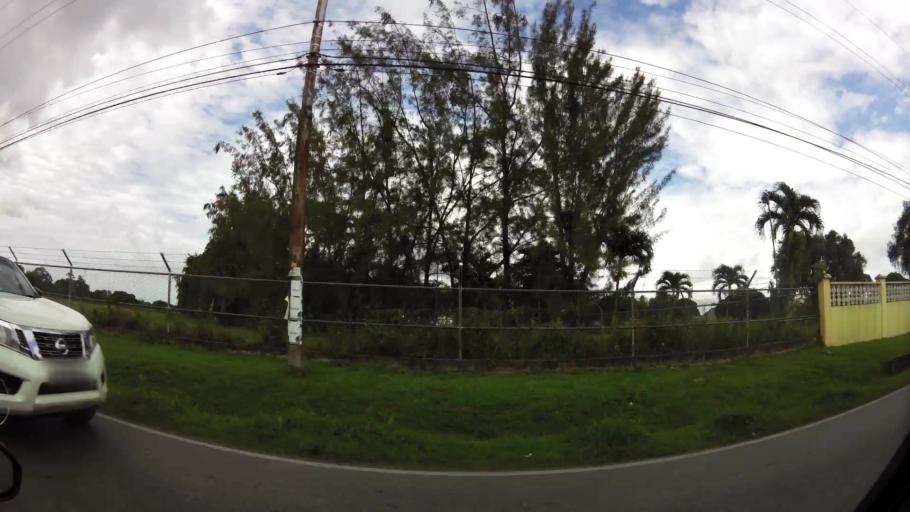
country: TT
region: Chaguanas
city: Chaguanas
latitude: 10.4662
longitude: -61.4181
